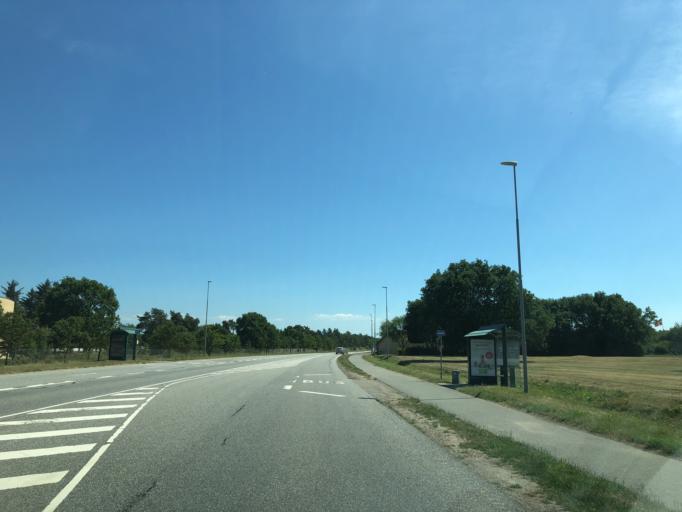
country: DK
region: Central Jutland
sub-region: Skive Kommune
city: Skive
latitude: 56.5414
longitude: 9.0351
